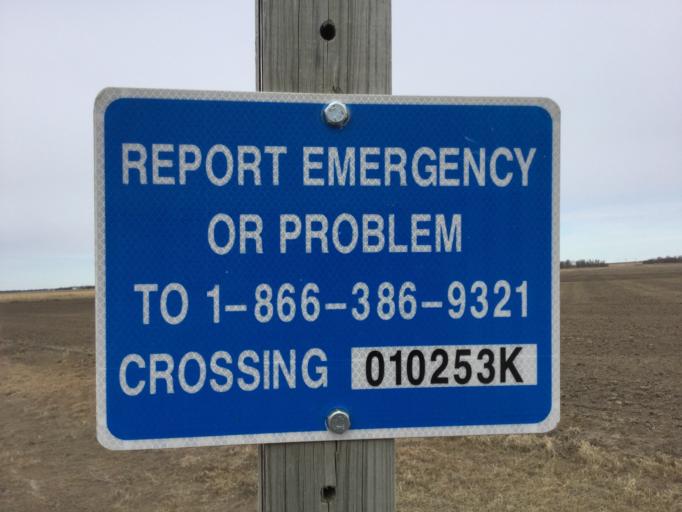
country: US
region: Kansas
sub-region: Rush County
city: La Crosse
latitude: 38.4643
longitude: -99.0496
